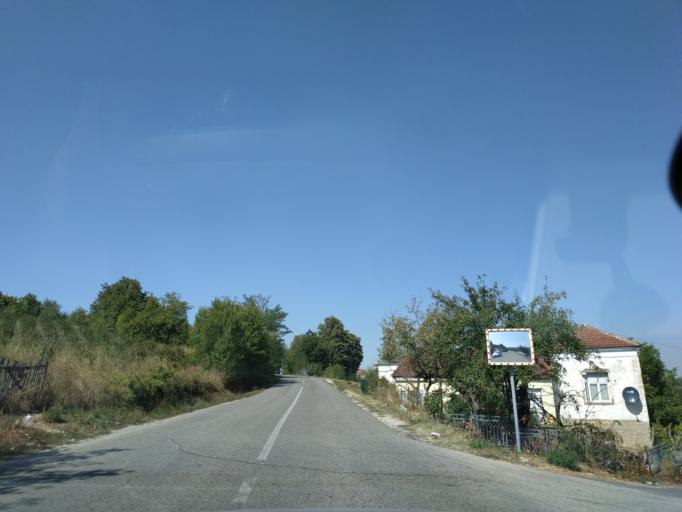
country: RS
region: Central Serbia
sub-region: Sumadijski Okrug
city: Topola
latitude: 44.2795
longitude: 20.6208
